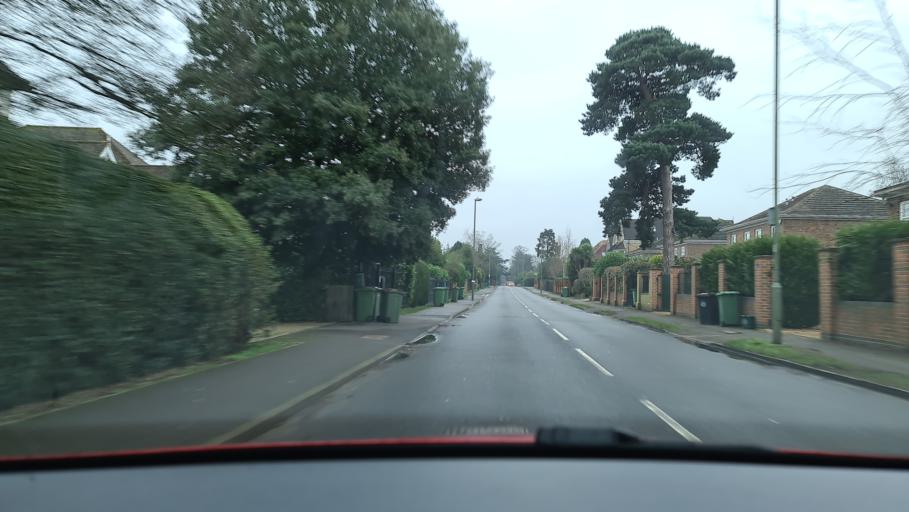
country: GB
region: England
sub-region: Surrey
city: Walton-on-Thames
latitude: 51.3770
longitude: -0.4331
